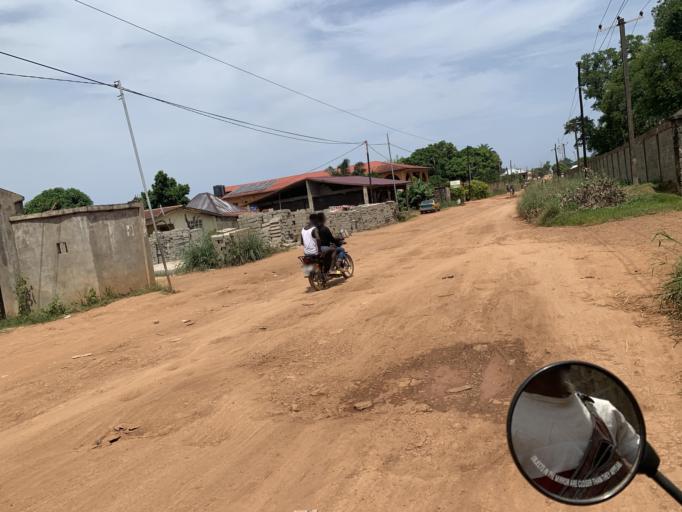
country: SL
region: Western Area
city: Hastings
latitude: 8.4024
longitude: -13.1372
